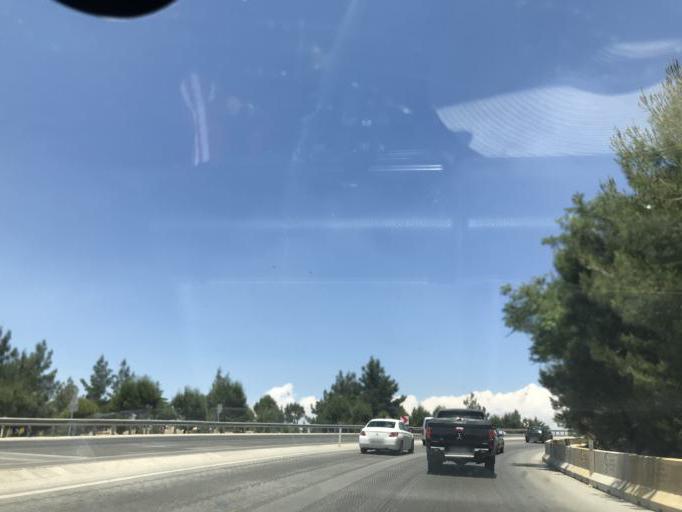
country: TR
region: Denizli
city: Denizli
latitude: 37.7305
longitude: 29.1720
